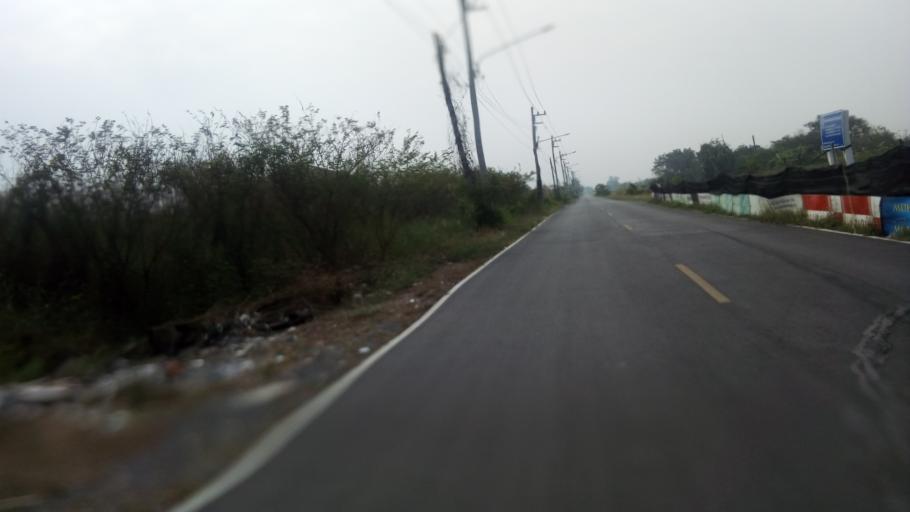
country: TH
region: Pathum Thani
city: Nong Suea
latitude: 14.0575
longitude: 100.8468
